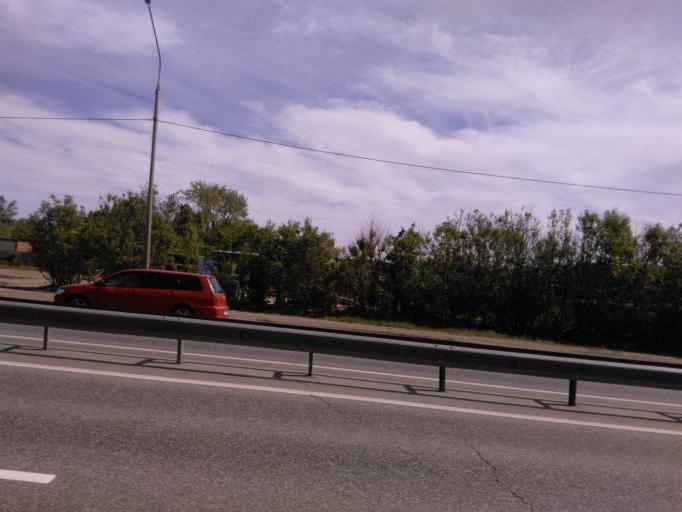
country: RU
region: Moskovskaya
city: Novopodrezkovo
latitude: 55.9438
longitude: 37.3598
